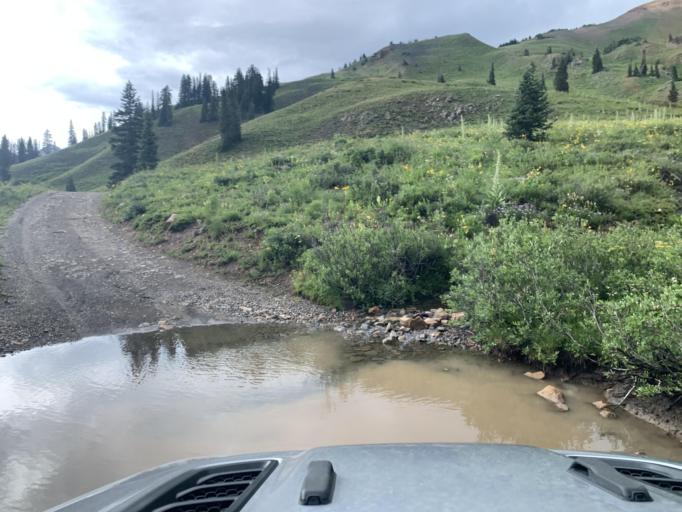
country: US
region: Colorado
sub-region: Gunnison County
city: Crested Butte
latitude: 38.9723
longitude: -107.0499
